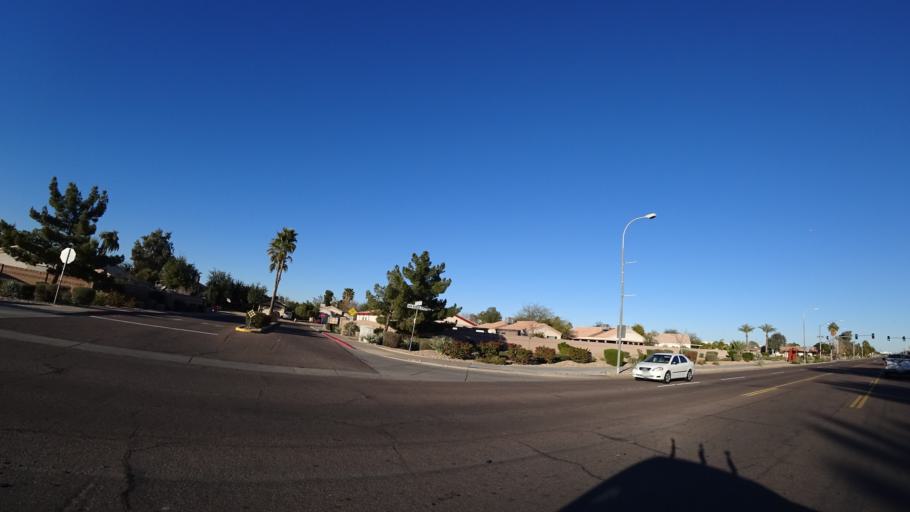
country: US
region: Arizona
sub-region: Maricopa County
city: Tolleson
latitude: 33.4509
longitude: -112.2482
